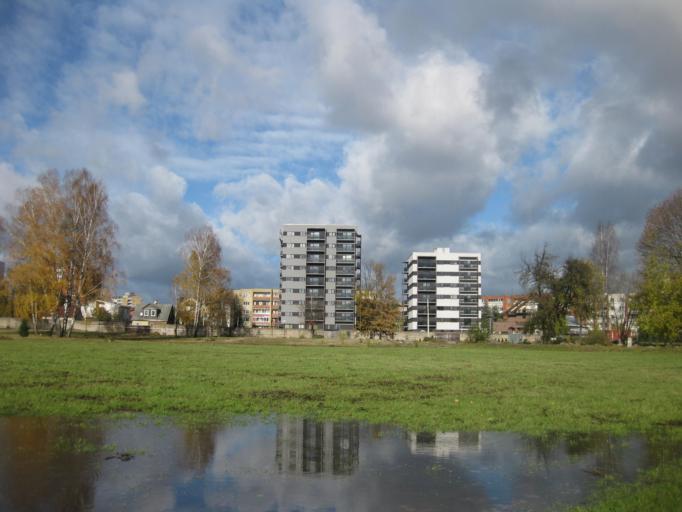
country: LT
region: Kauno apskritis
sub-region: Kaunas
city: Eiguliai
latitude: 54.9078
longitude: 23.9431
